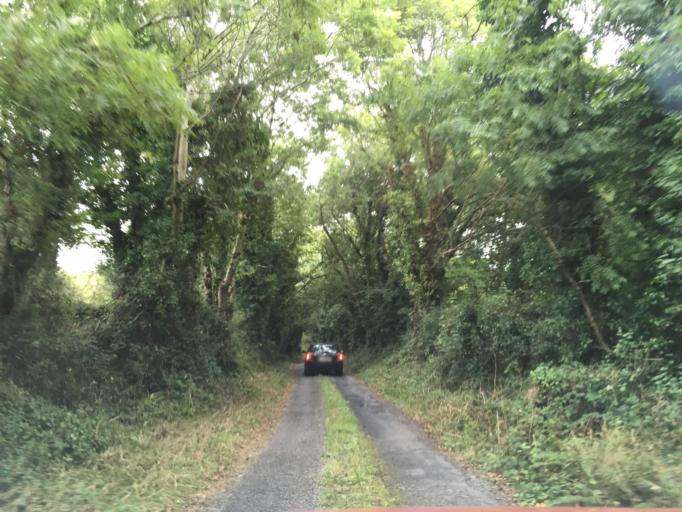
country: IE
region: Munster
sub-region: County Limerick
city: Askeaton
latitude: 52.7162
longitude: -9.0591
